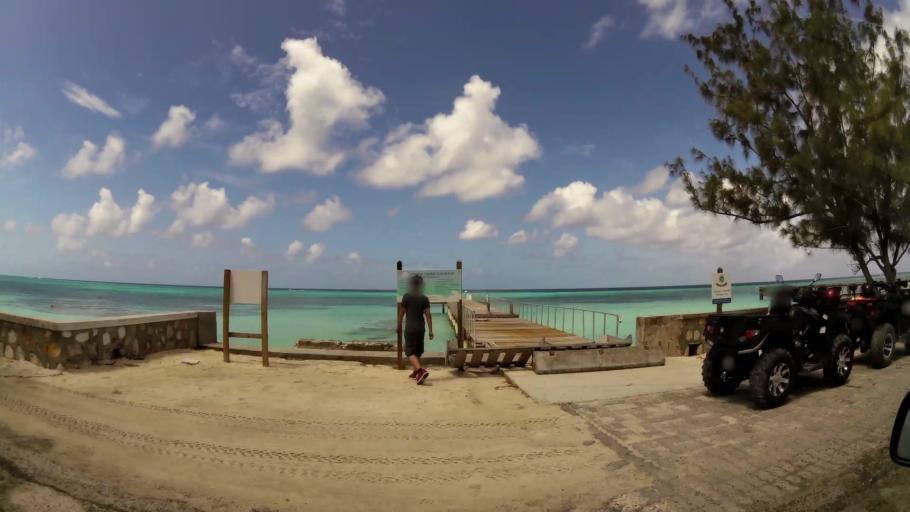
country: TC
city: Cockburn Town
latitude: 21.4692
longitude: -71.1468
